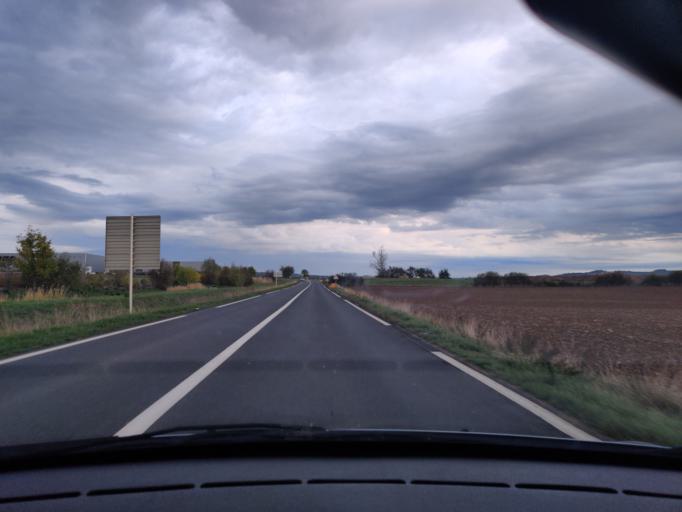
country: FR
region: Auvergne
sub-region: Departement du Puy-de-Dome
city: Combronde
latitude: 45.9947
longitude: 3.0906
